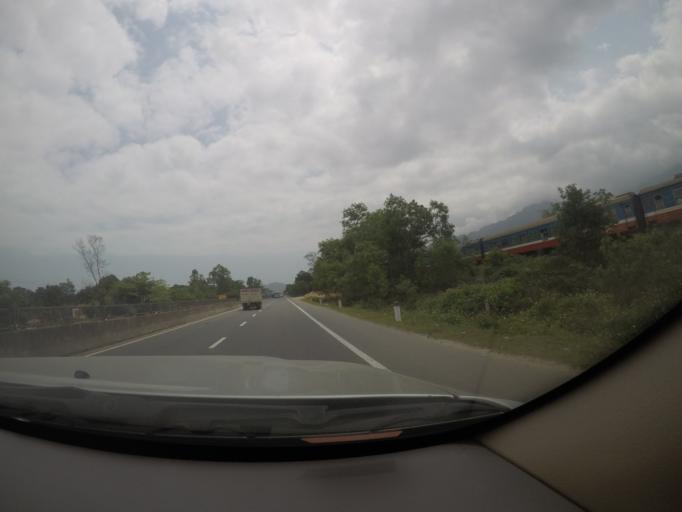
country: VN
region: Thua Thien-Hue
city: Phu Loc
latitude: 16.2718
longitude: 107.9749
